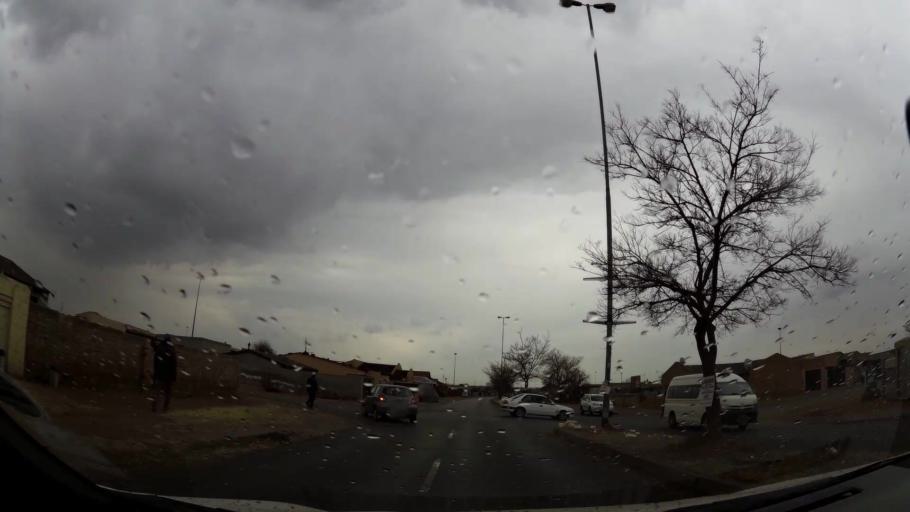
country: ZA
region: Gauteng
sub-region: Ekurhuleni Metropolitan Municipality
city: Germiston
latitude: -26.3335
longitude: 28.1497
